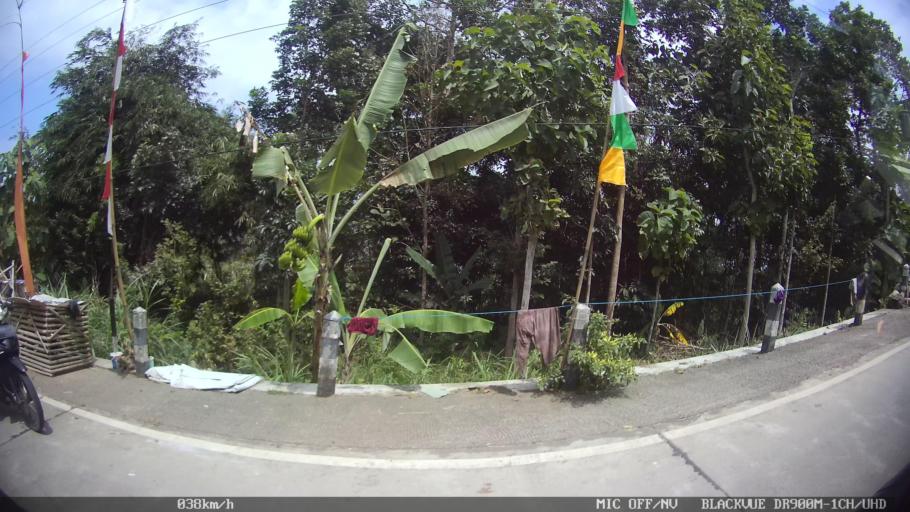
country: ID
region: Central Java
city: Candi Prambanan
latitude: -7.7857
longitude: 110.5148
